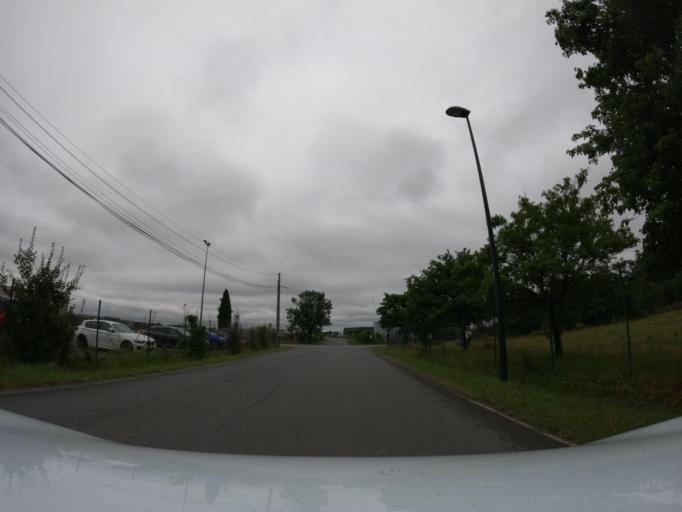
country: FR
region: Pays de la Loire
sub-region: Departement de la Vendee
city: Maillezais
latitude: 46.4231
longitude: -0.7090
